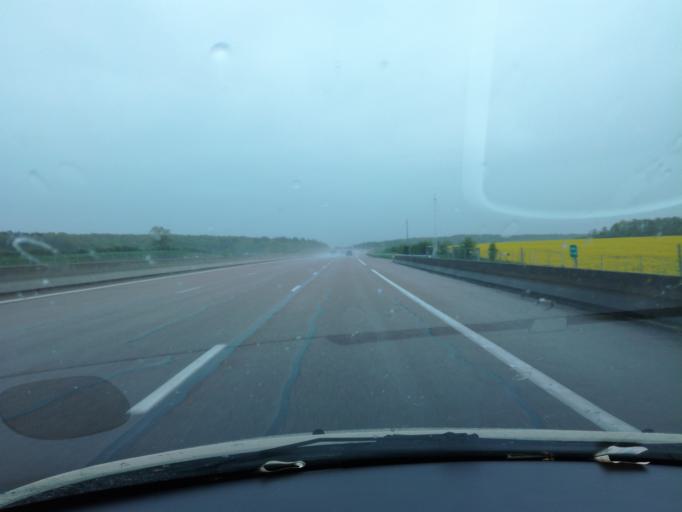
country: FR
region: Champagne-Ardenne
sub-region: Departement de la Haute-Marne
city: Rolampont
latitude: 47.8867
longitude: 5.2228
